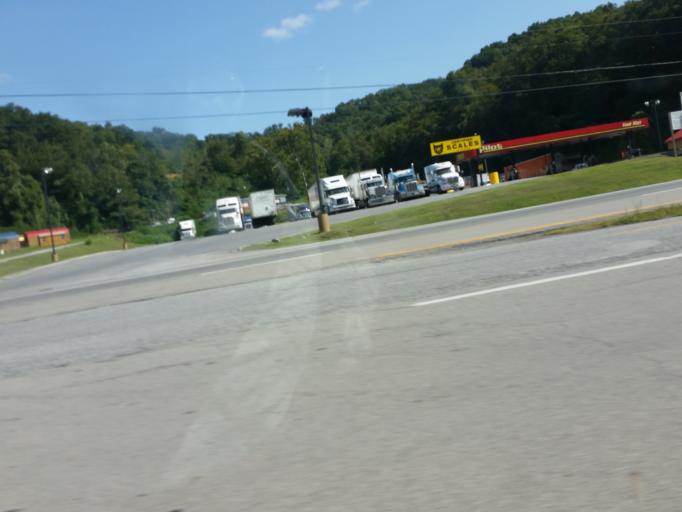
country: US
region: Kentucky
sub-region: Bell County
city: Middlesboro
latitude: 36.6440
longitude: -83.7008
